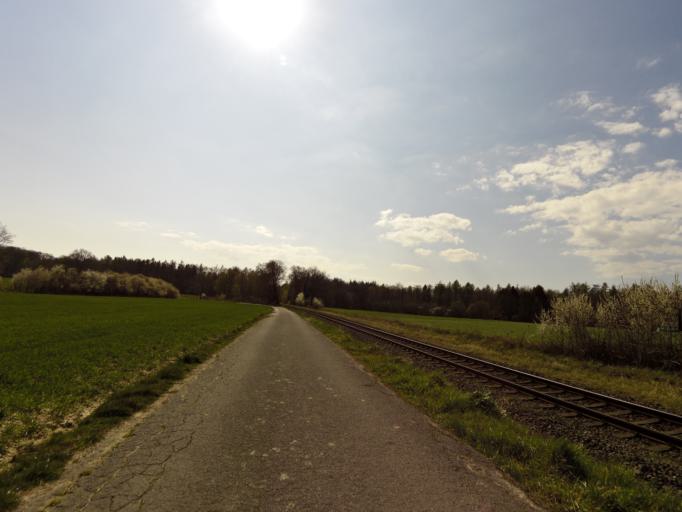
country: DE
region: North Rhine-Westphalia
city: Meckenheim
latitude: 50.6706
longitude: 7.0199
